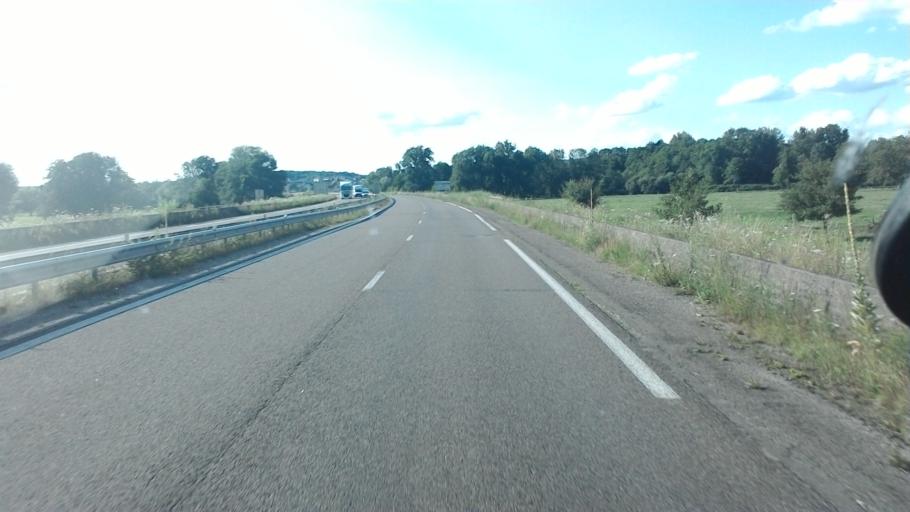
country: FR
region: Franche-Comte
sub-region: Departement de la Haute-Saone
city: Froideconche
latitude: 47.8097
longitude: 6.4030
